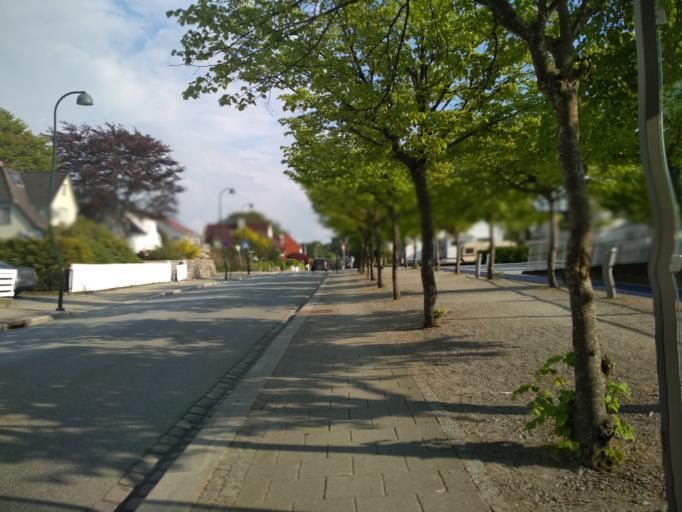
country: NO
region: Rogaland
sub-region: Stavanger
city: Stavanger
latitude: 58.9649
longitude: 5.7130
